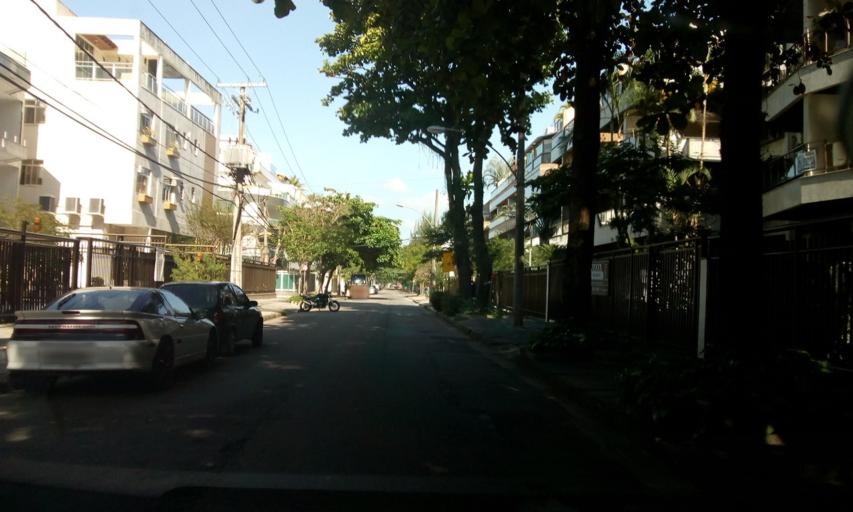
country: BR
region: Rio de Janeiro
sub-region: Rio De Janeiro
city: Rio de Janeiro
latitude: -23.0135
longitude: -43.3009
